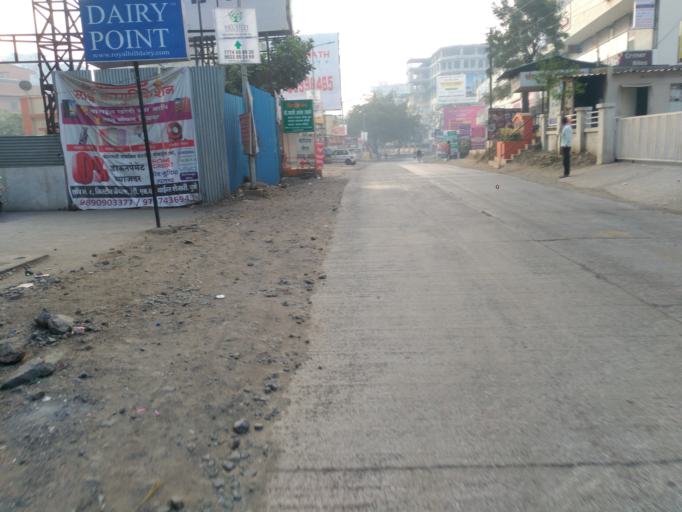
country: IN
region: Maharashtra
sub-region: Pune Division
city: Pune
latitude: 18.4556
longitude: 73.9135
